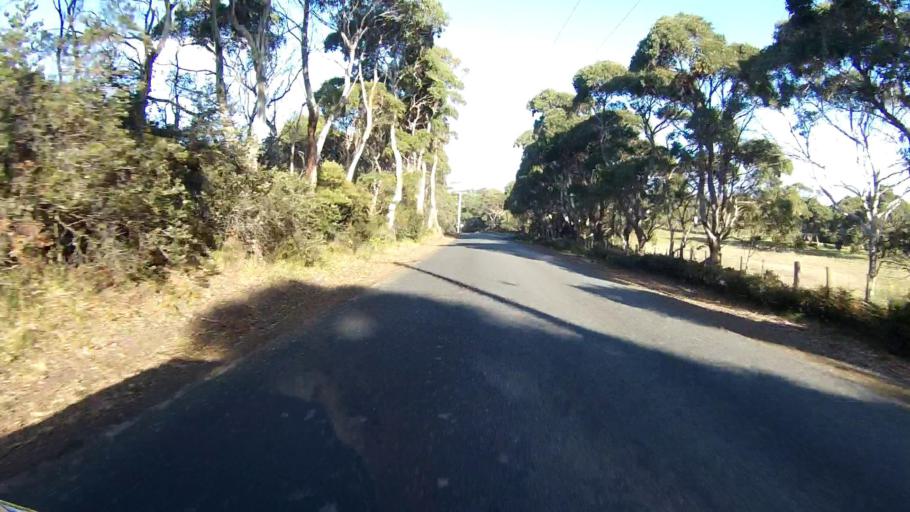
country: AU
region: Tasmania
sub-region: Clarence
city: Sandford
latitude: -43.1805
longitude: 147.8527
